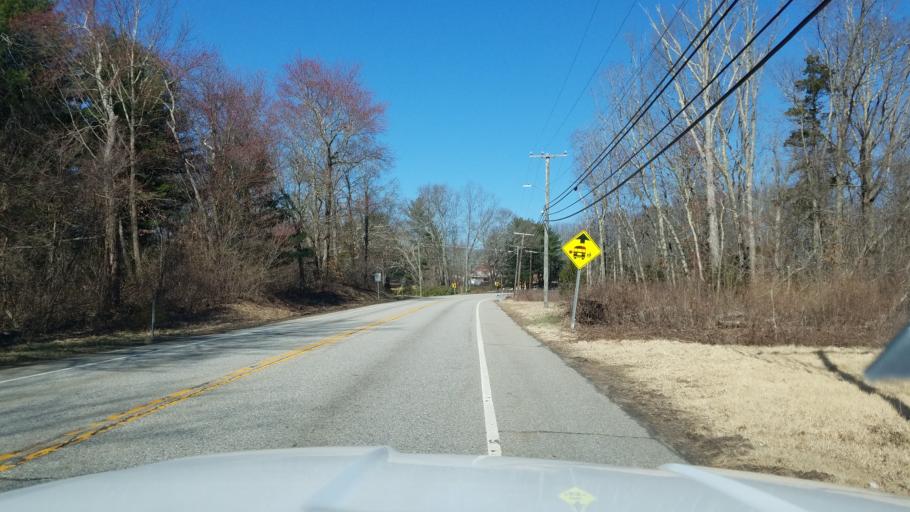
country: US
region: Connecticut
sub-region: Tolland County
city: Mansfield City
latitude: 41.7339
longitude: -72.2536
